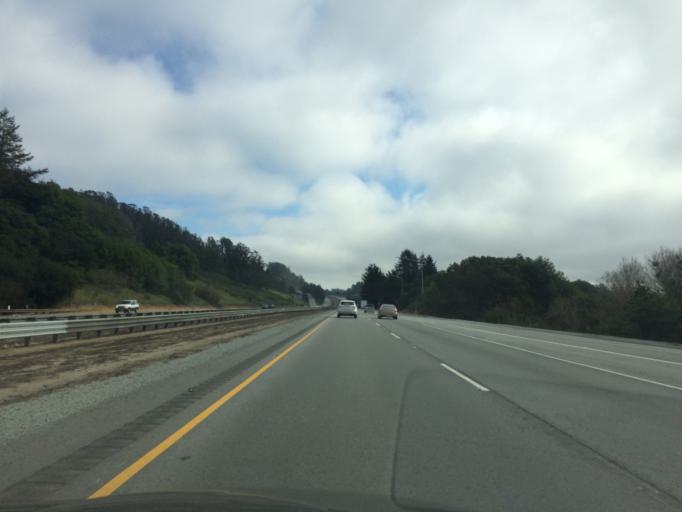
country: US
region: California
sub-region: Santa Cruz County
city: La Selva Beach
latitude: 36.9585
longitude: -121.8605
